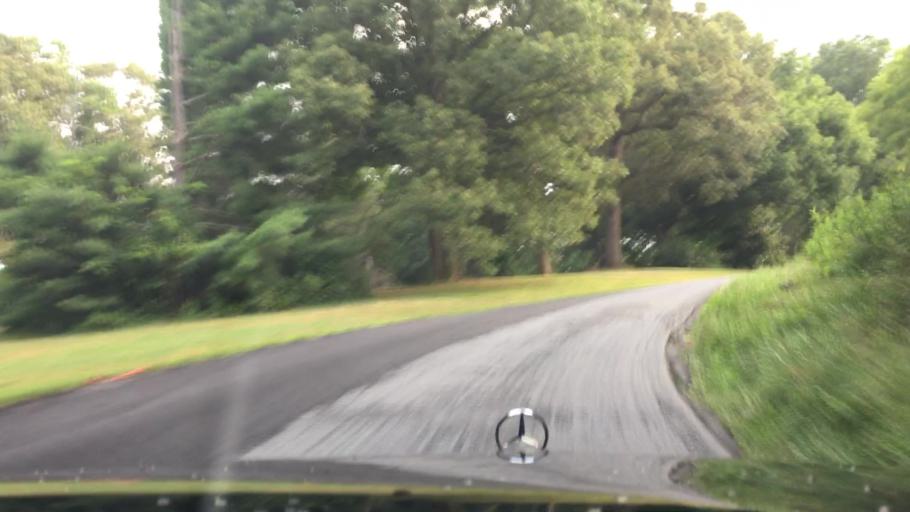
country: US
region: Virginia
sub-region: Campbell County
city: Timberlake
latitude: 37.2587
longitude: -79.3151
